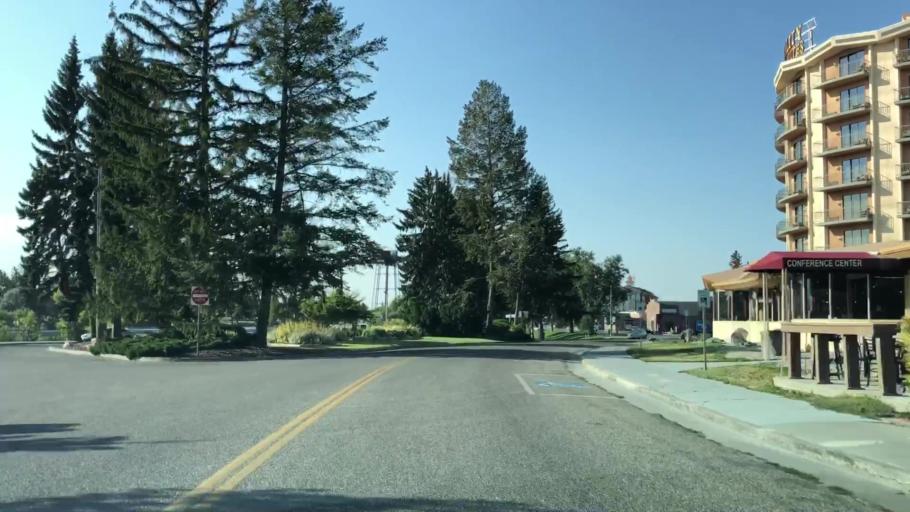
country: US
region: Idaho
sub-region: Bonneville County
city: Idaho Falls
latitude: 43.4971
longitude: -112.0441
